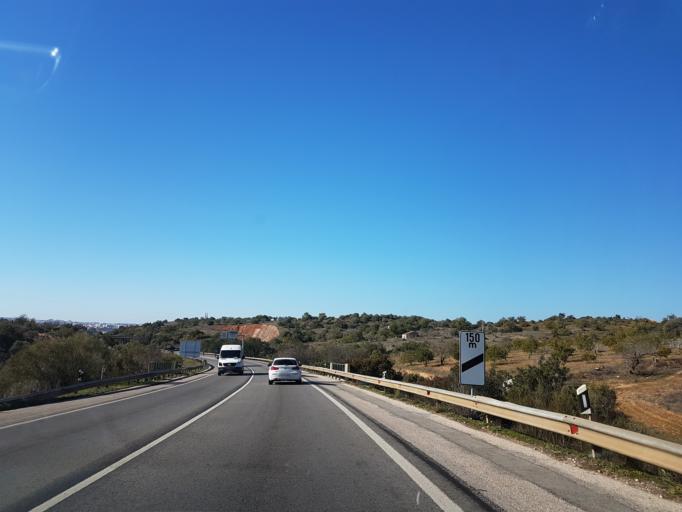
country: PT
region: Faro
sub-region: Lagoa
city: Estombar
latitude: 37.1533
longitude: -8.4907
